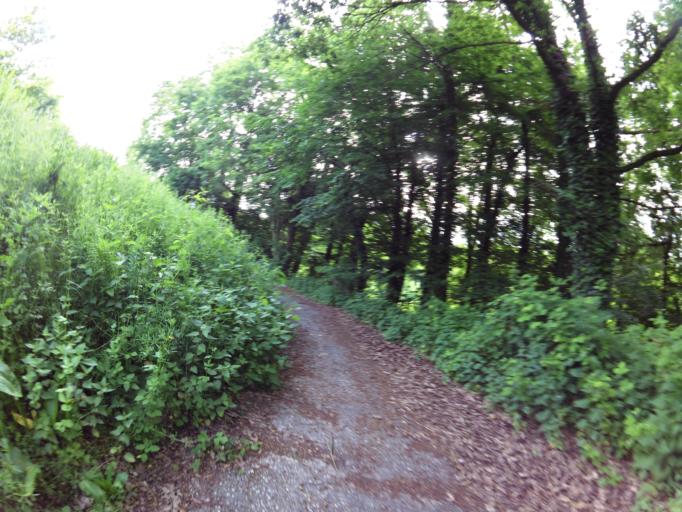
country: DE
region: North Rhine-Westphalia
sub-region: Regierungsbezirk Koln
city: Ubach-Palenberg
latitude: 50.9133
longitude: 6.0766
